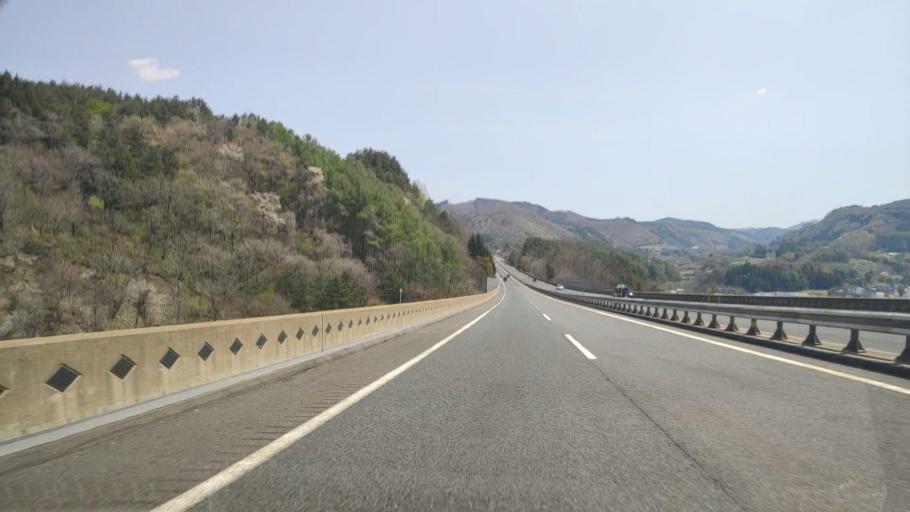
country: JP
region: Iwate
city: Ichinohe
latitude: 40.2287
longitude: 141.2810
